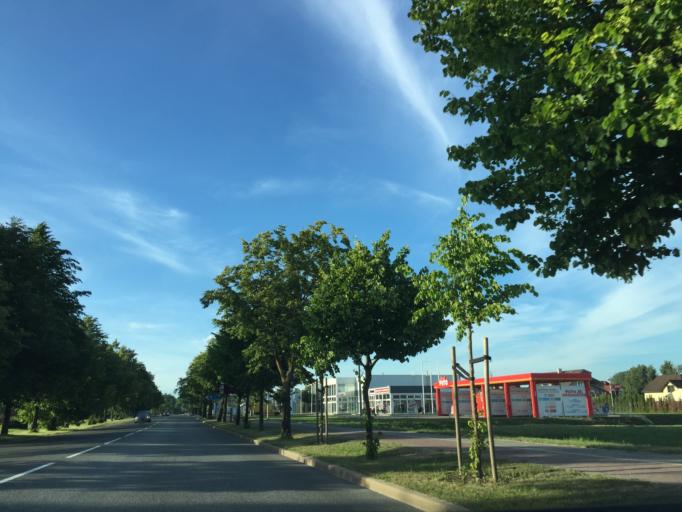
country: LV
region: Ventspils
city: Ventspils
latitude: 57.3766
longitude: 21.5659
